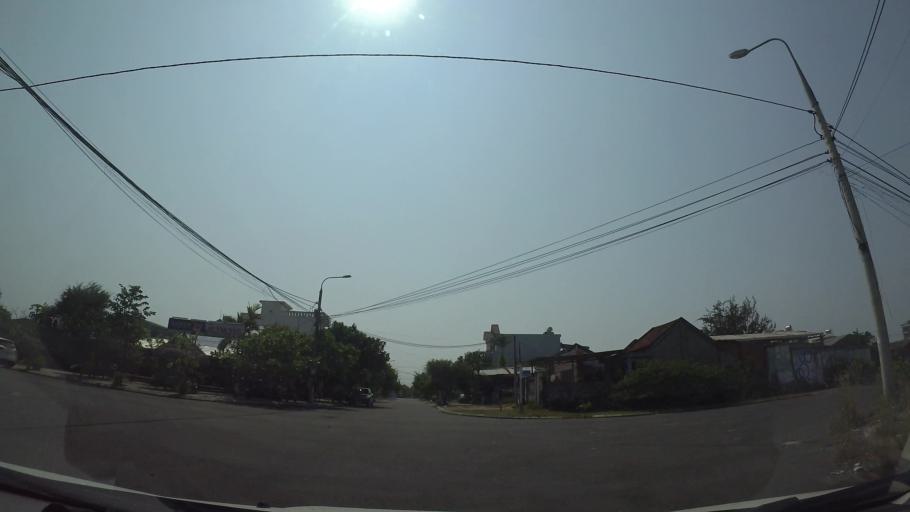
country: VN
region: Da Nang
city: Ngu Hanh Son
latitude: 16.0099
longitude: 108.2618
